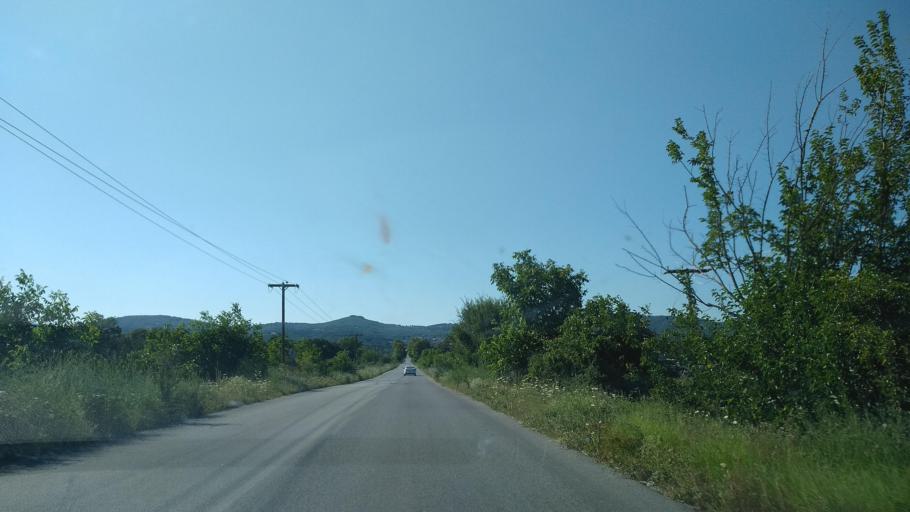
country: GR
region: Central Macedonia
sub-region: Nomos Chalkidikis
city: Megali Panagia
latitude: 40.4196
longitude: 23.6895
